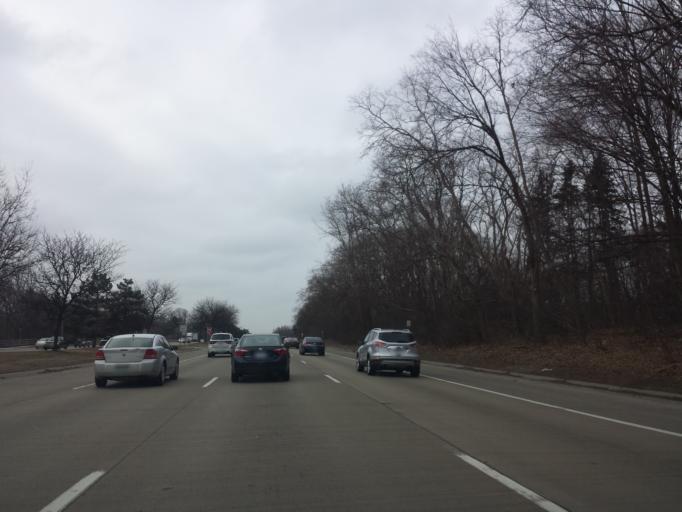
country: US
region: Michigan
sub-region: Oakland County
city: Bloomfield Hills
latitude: 42.5918
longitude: -83.2817
